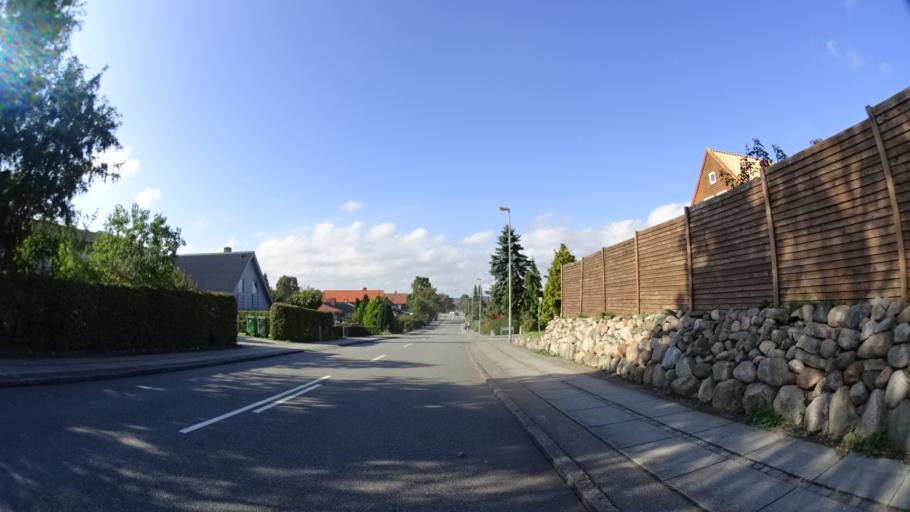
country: DK
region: Central Jutland
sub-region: Arhus Kommune
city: Stavtrup
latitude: 56.1163
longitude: 10.1667
